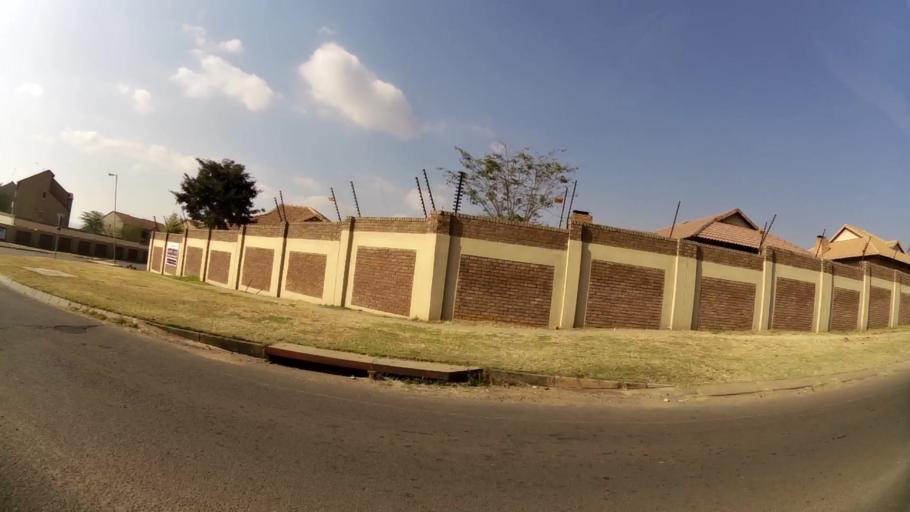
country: ZA
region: Gauteng
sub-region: City of Tshwane Metropolitan Municipality
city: Pretoria
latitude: -25.7810
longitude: 28.3497
